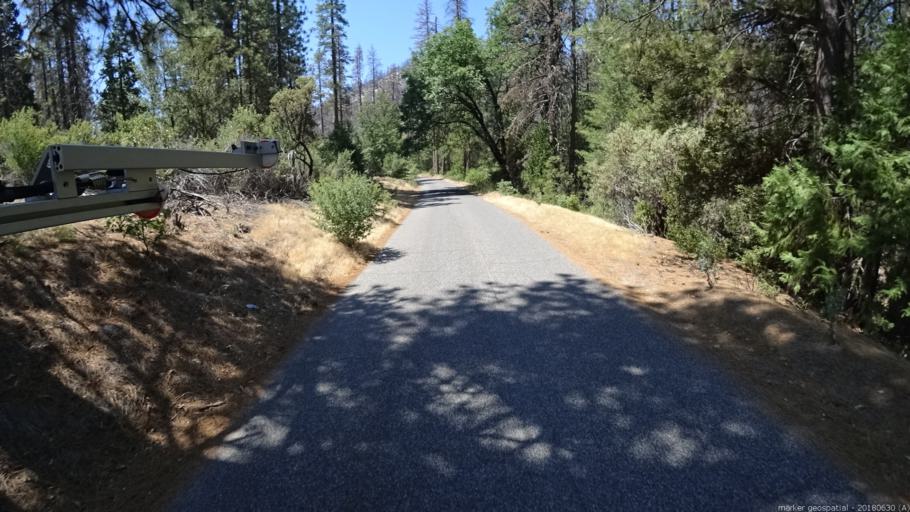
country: US
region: California
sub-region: Madera County
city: Oakhurst
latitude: 37.3571
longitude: -119.3445
